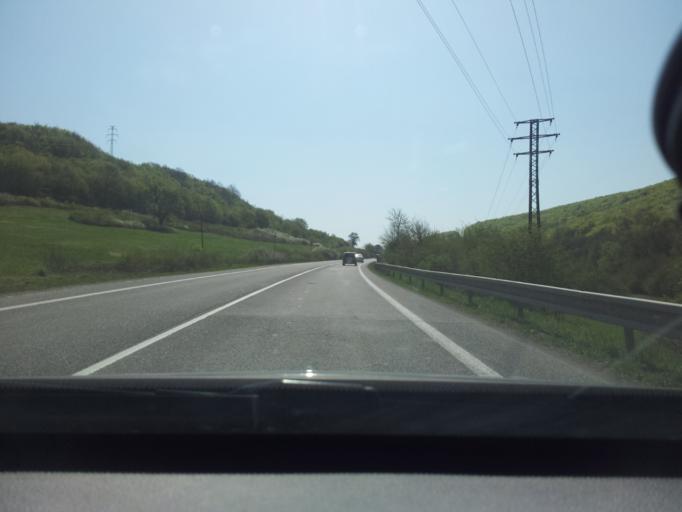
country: SK
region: Trenciansky
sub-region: Okres Trencin
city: Trencin
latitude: 48.8228
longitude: 18.0740
